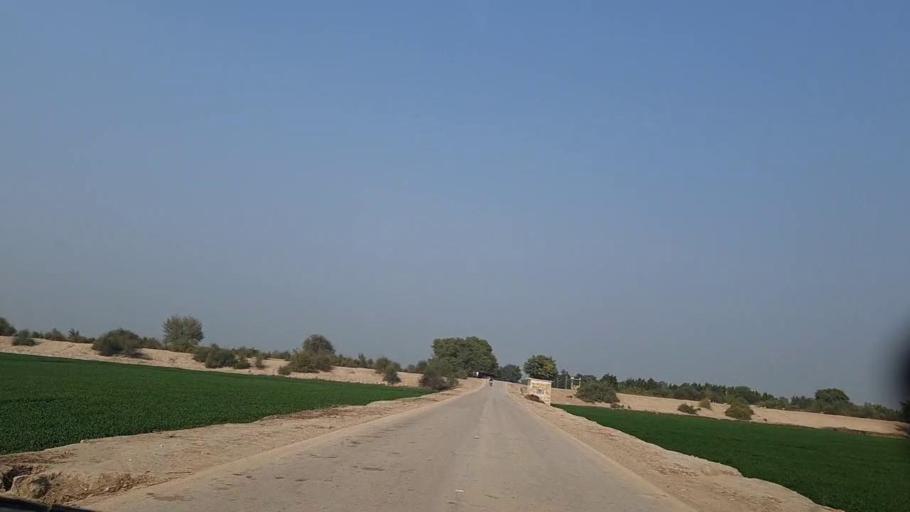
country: PK
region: Sindh
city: Sann
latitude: 26.1763
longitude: 68.1073
